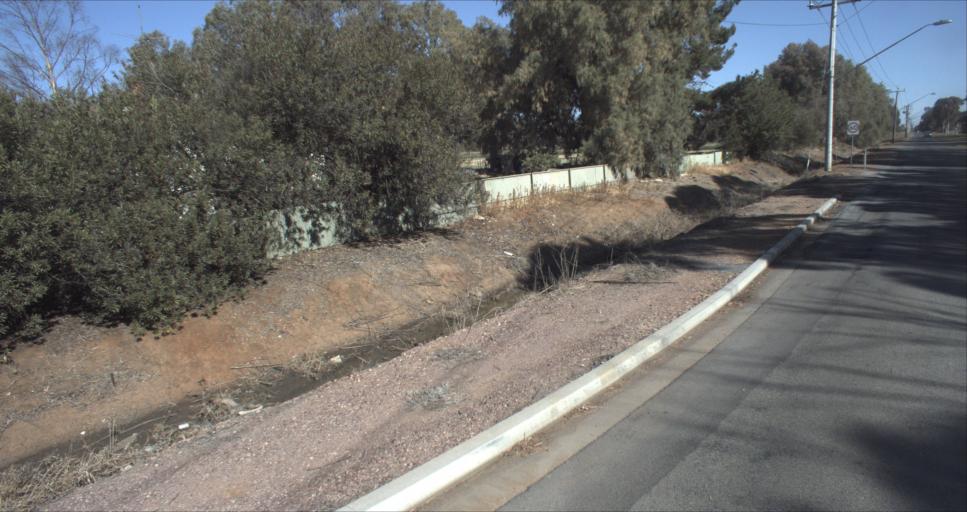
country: AU
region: New South Wales
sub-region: Leeton
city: Leeton
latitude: -34.5637
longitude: 146.4148
